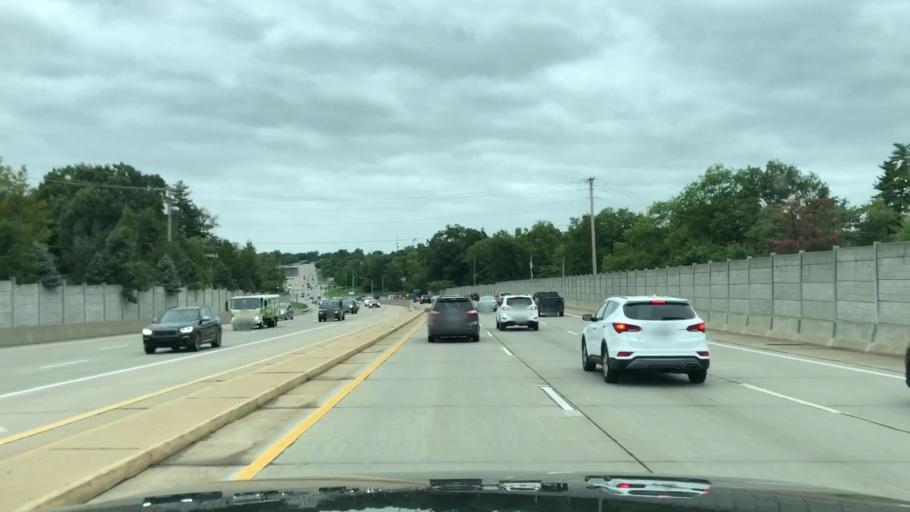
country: US
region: Missouri
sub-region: Saint Louis County
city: Manchester
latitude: 38.6055
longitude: -90.5104
